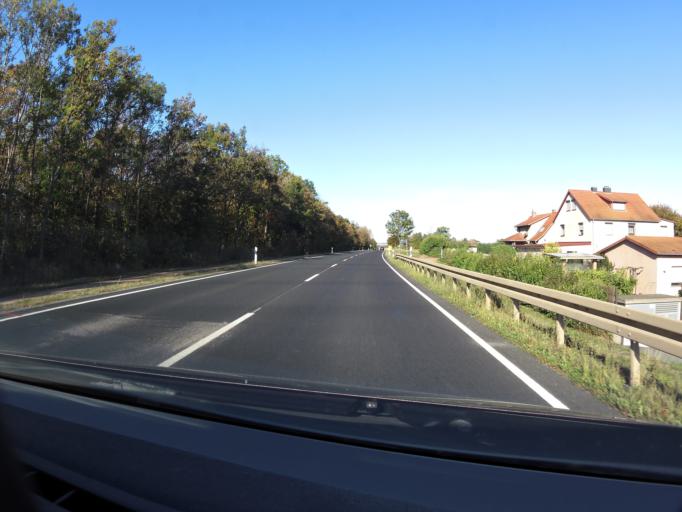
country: DE
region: Saxony-Anhalt
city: Ditfurt
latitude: 51.8002
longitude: 11.1873
